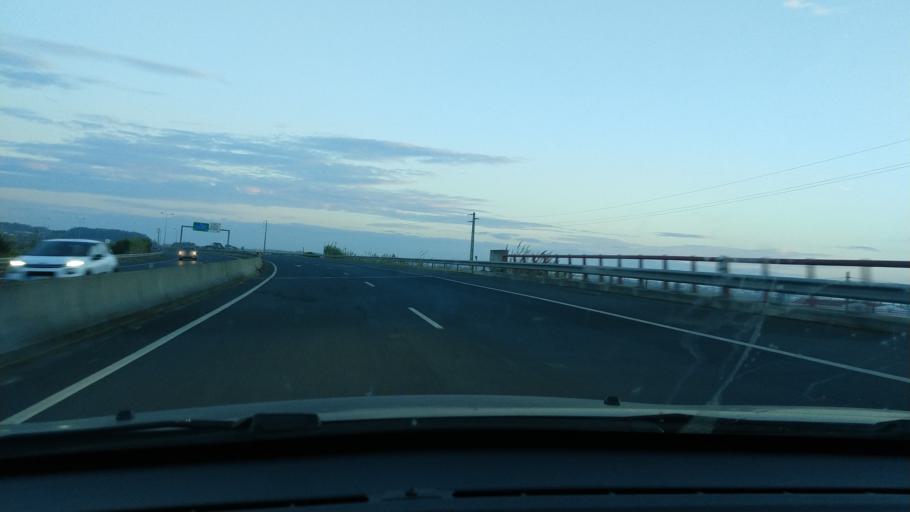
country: PT
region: Leiria
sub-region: Peniche
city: Atouguia da Baleia
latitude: 39.3335
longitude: -9.3349
